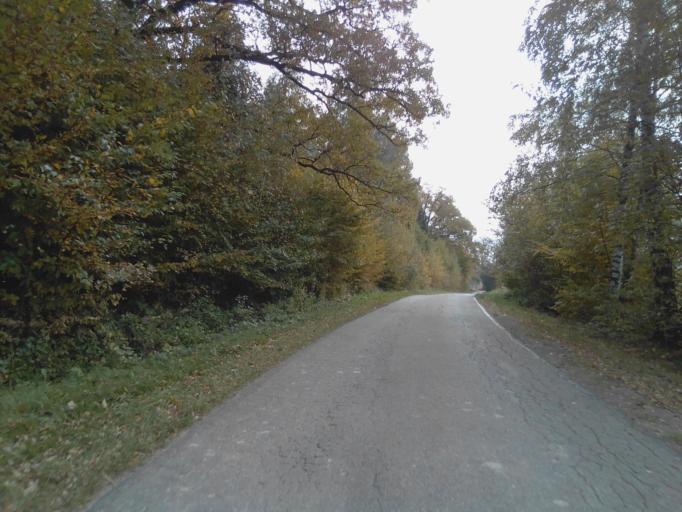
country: PL
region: Subcarpathian Voivodeship
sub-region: Powiat rzeszowski
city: Straszydle
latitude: 49.8615
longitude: 21.9739
